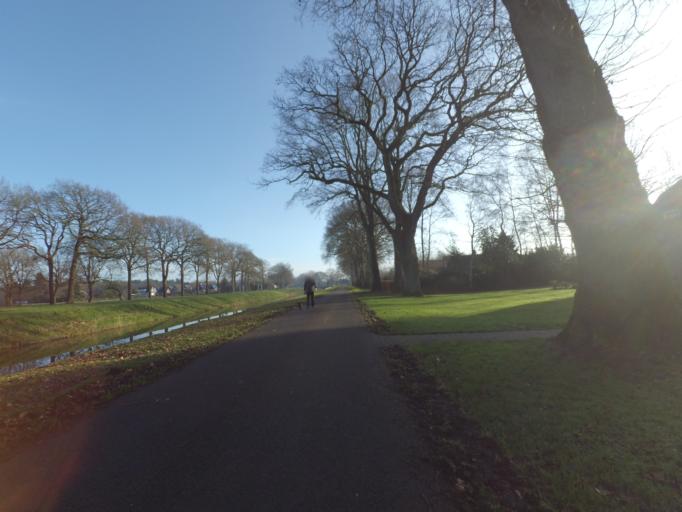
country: NL
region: Drenthe
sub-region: Gemeente Coevorden
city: Sleen
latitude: 52.8418
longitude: 6.7166
